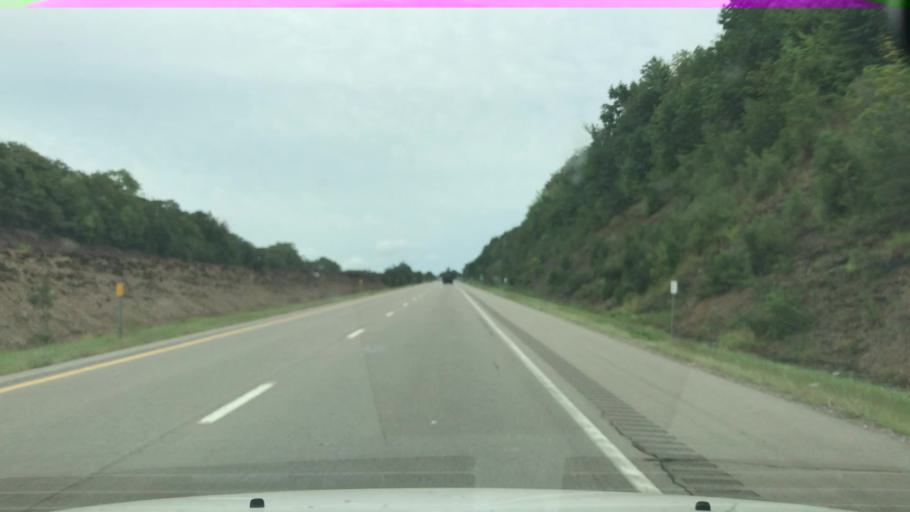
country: US
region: New York
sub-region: Erie County
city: North Boston
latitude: 42.6716
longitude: -78.7782
